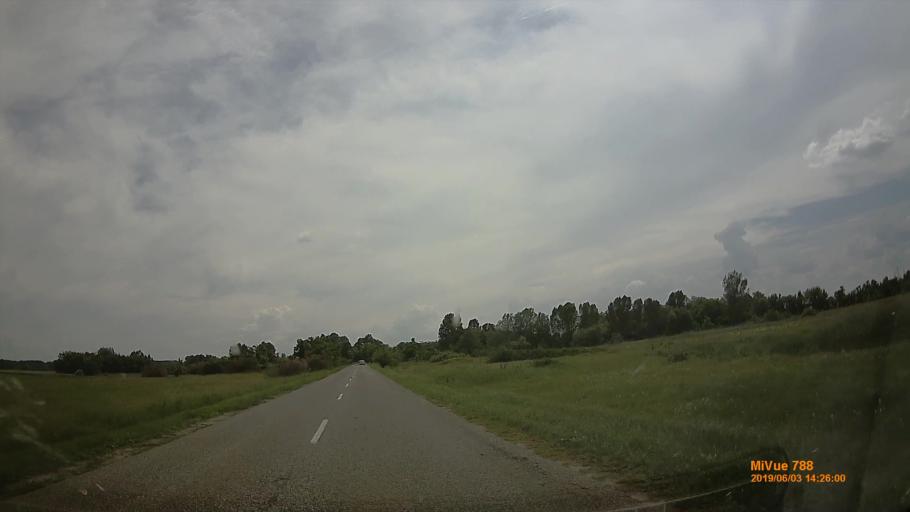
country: HU
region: Bacs-Kiskun
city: Tiszakecske
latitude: 46.9972
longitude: 20.1253
